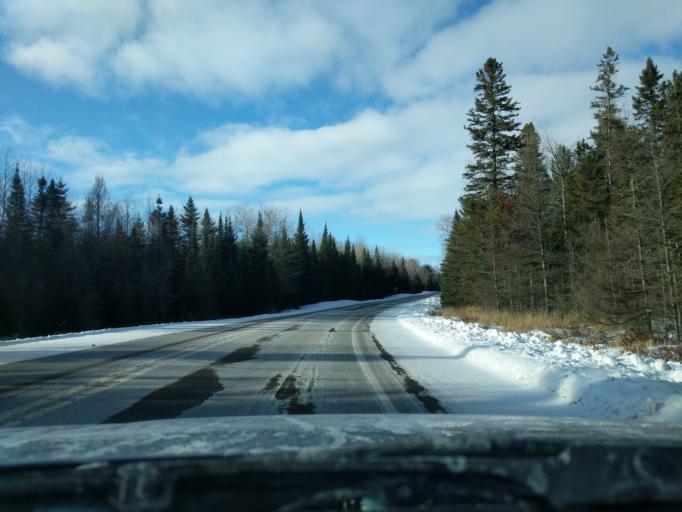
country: US
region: Wisconsin
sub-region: Vilas County
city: Eagle River
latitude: 45.7626
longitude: -89.0646
